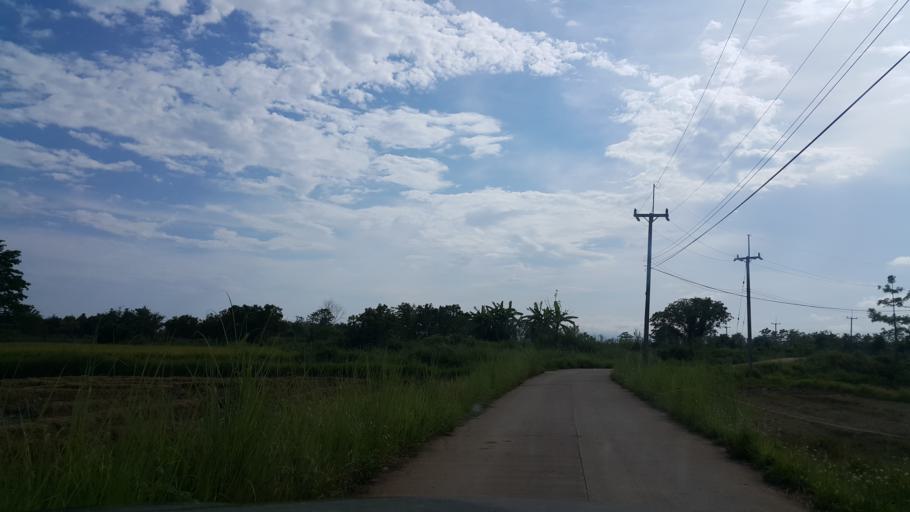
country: TH
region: Chiang Rai
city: Chiang Rai
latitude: 19.9720
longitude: 99.9005
